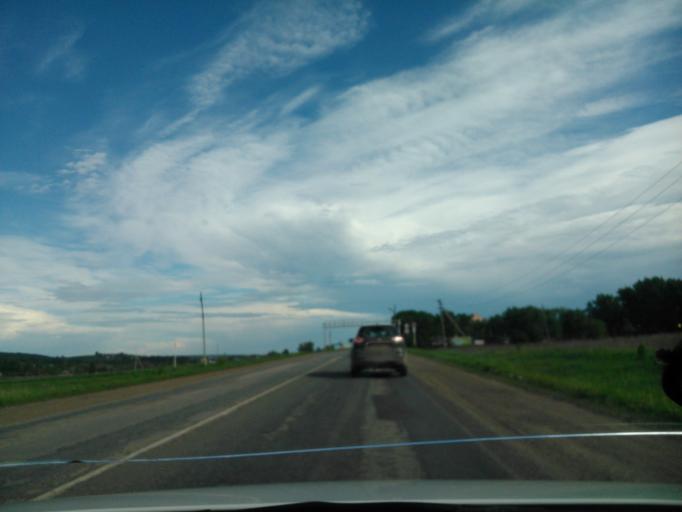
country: RU
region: Perm
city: Lobanovo
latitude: 57.8687
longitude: 56.2867
